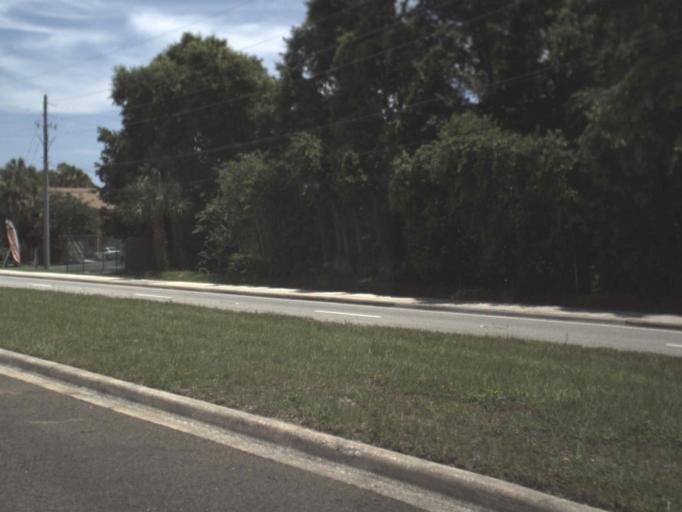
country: US
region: Florida
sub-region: Duval County
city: Jacksonville
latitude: 30.3273
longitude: -81.6009
